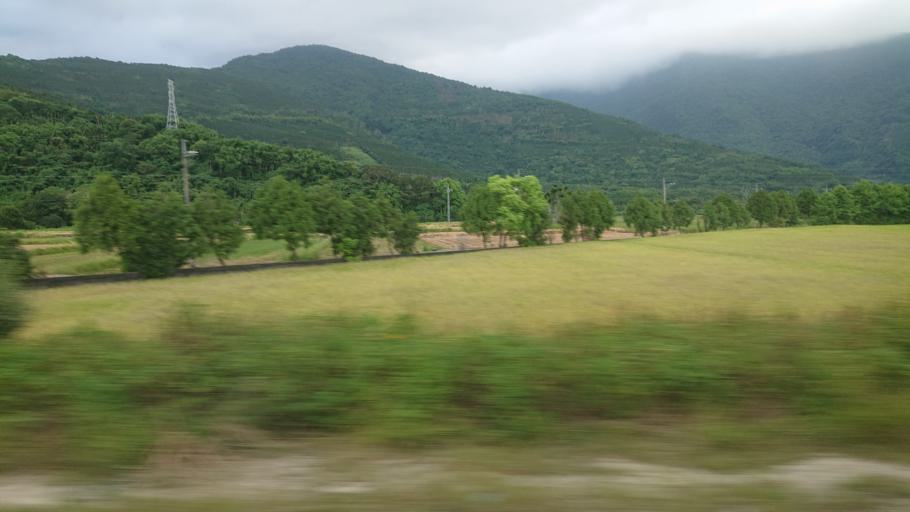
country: TW
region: Taiwan
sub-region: Hualien
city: Hualian
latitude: 23.7352
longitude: 121.4412
